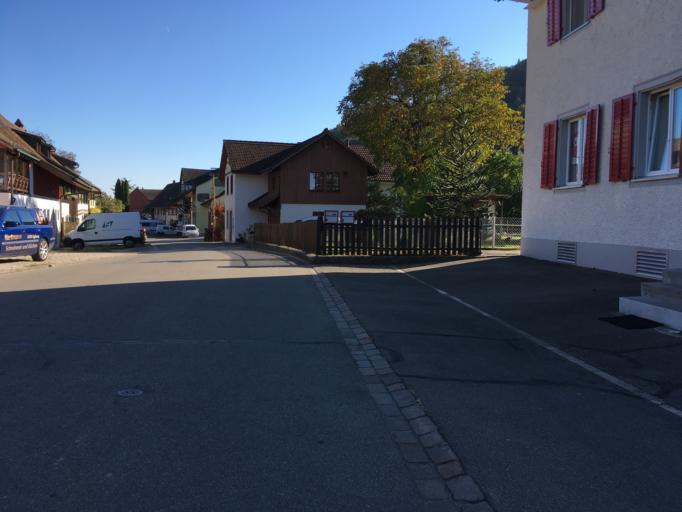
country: CH
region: Zurich
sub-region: Bezirk Buelach
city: Seglingen
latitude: 47.5664
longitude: 8.5427
